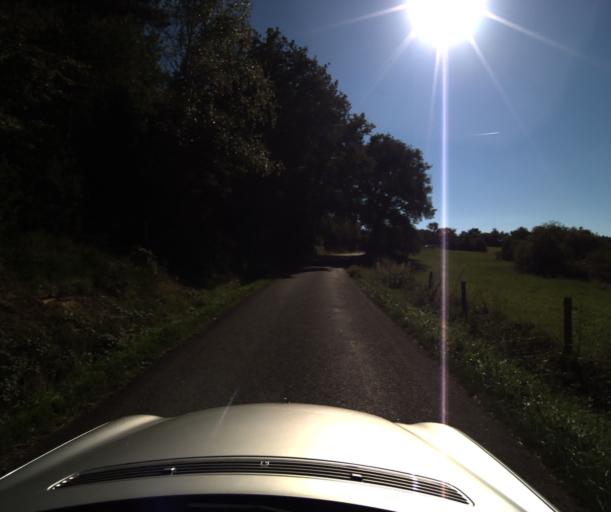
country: FR
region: Midi-Pyrenees
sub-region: Departement de l'Ariege
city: Lavelanet
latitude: 42.9804
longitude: 1.8830
